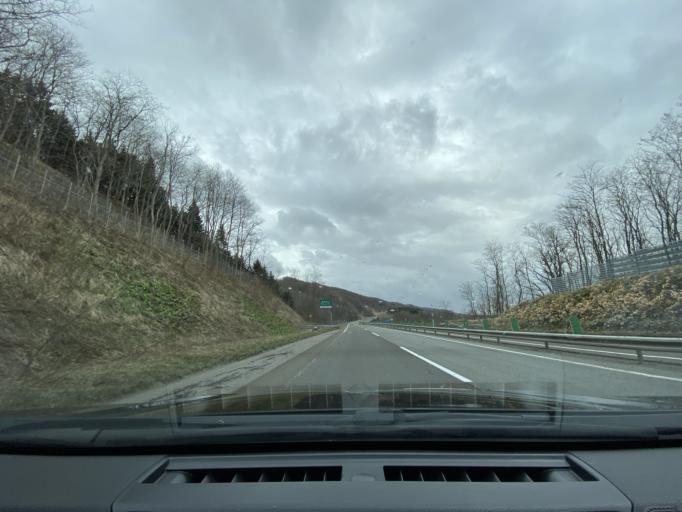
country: JP
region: Hokkaido
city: Sunagawa
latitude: 43.4196
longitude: 141.9111
